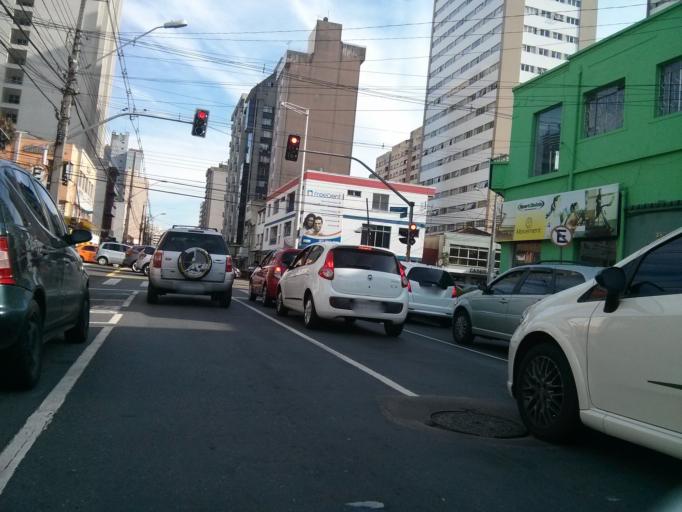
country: BR
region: Parana
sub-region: Curitiba
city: Curitiba
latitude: -25.4415
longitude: -49.2712
